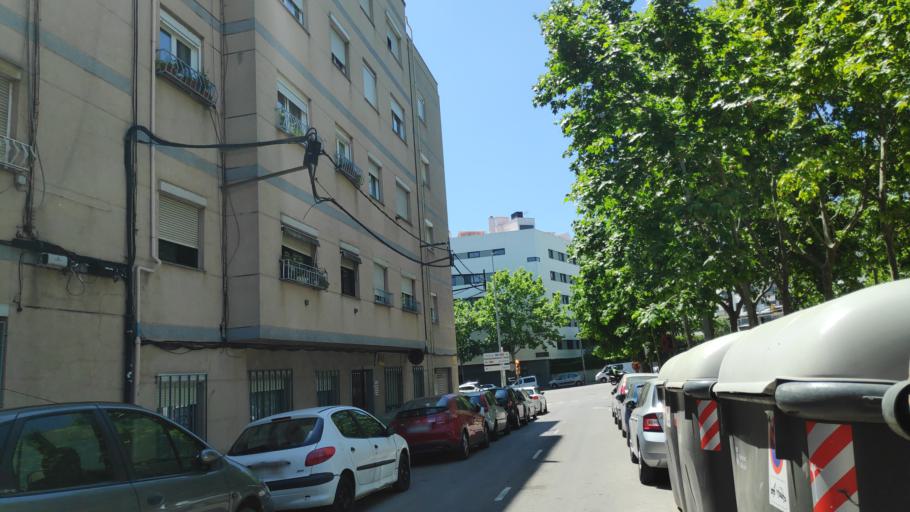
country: ES
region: Catalonia
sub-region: Provincia de Barcelona
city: Sant Quirze del Valles
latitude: 41.5505
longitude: 2.0801
